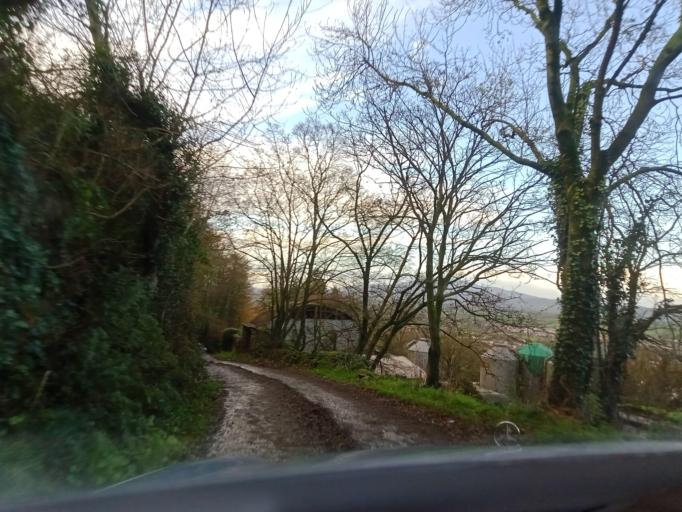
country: IE
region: Munster
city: Carrick-on-Suir
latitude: 52.3373
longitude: -7.4097
